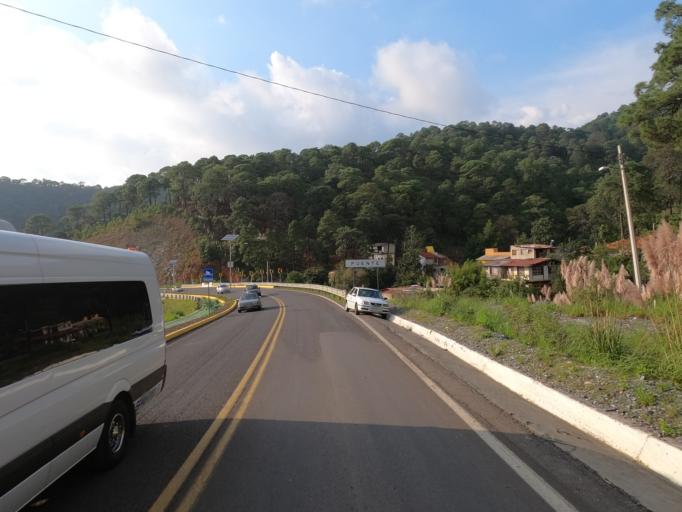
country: MX
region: Mexico
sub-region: Valle de Bravo
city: Colonia Rincon Villa del Valle
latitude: 19.2091
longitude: -100.1080
